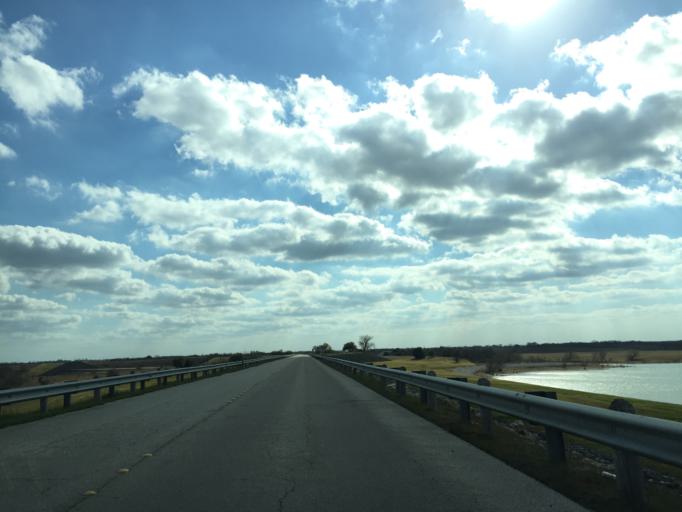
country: US
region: Texas
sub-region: Williamson County
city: Granger
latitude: 30.6893
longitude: -97.3358
